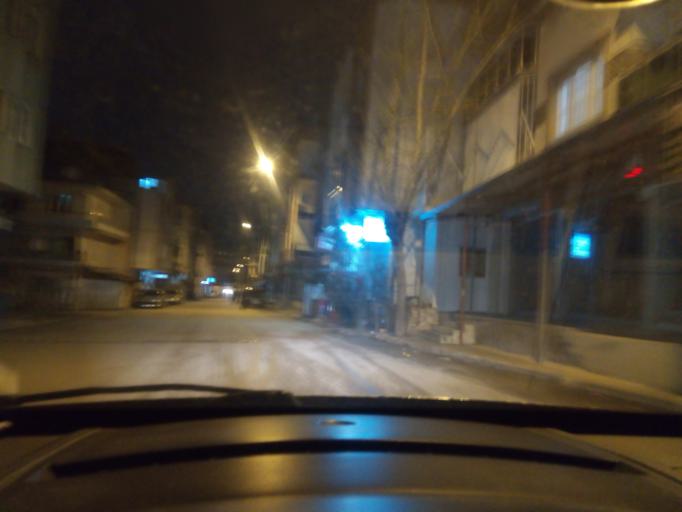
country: TR
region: Bursa
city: Niluefer
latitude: 40.2585
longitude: 28.9585
